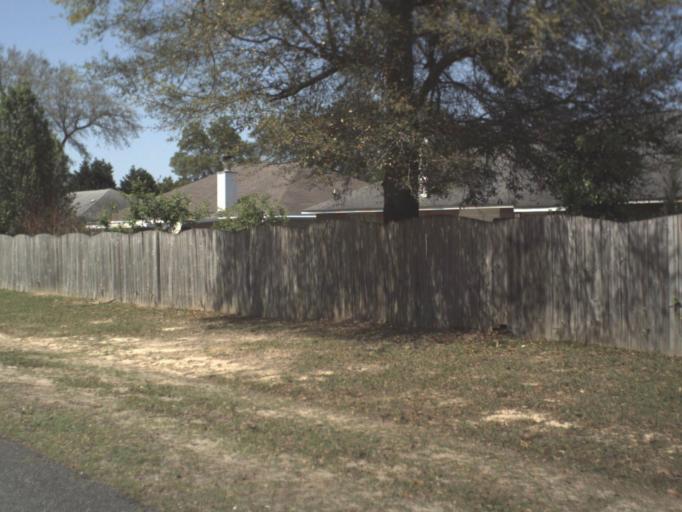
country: US
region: Florida
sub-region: Escambia County
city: Bellview
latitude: 30.4898
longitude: -87.3197
